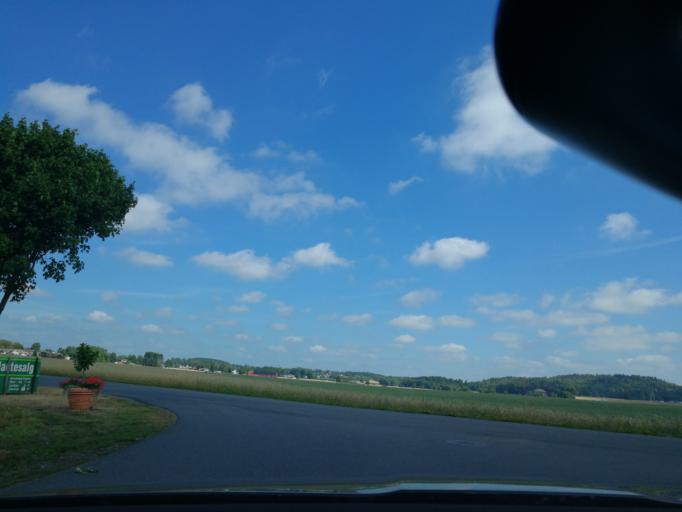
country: NO
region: Vestfold
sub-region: Sandefjord
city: Sandefjord
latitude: 59.1536
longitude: 10.2022
